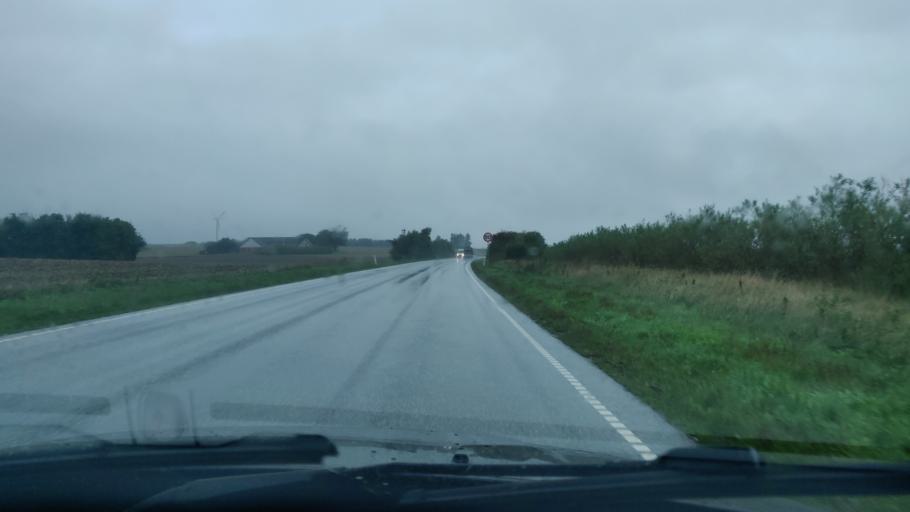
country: DK
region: North Denmark
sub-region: Thisted Kommune
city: Thisted
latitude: 56.9663
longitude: 8.6524
